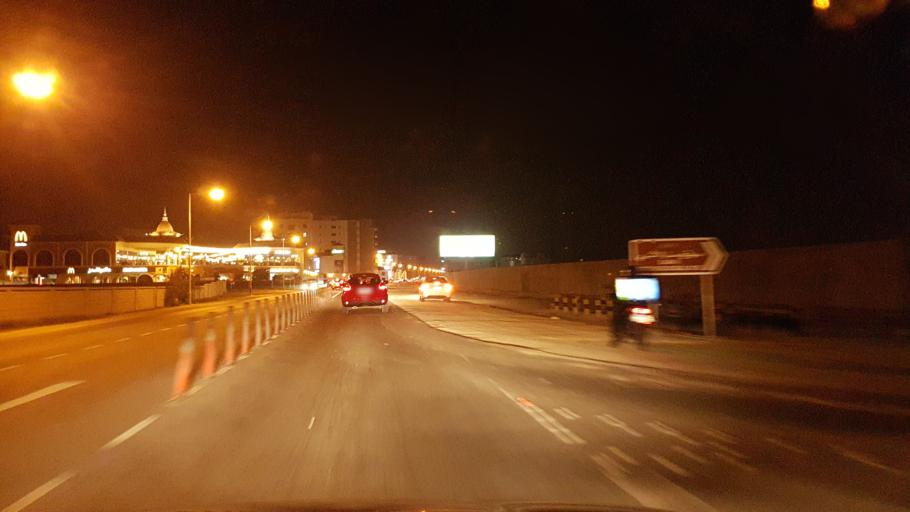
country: BH
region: Northern
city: Madinat `Isa
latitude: 26.1772
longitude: 50.4810
